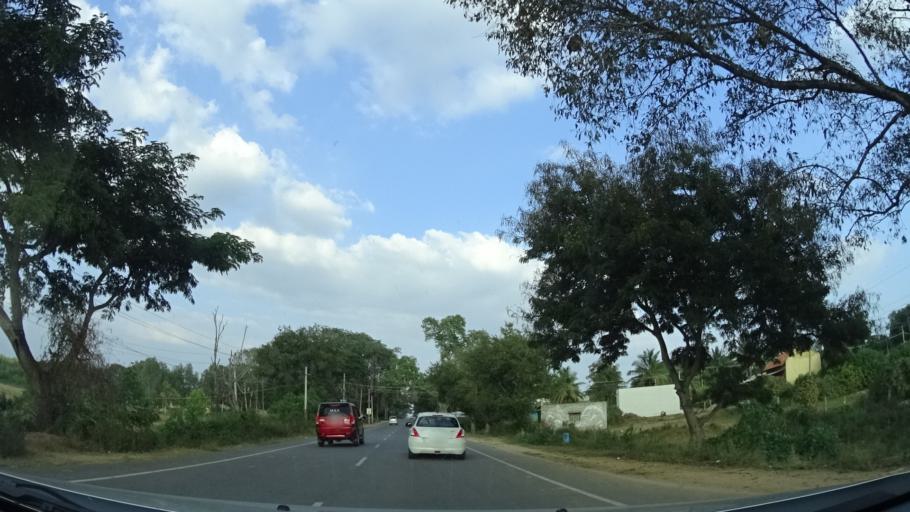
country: IN
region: Karnataka
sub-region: Mandya
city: Malavalli
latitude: 12.3757
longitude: 77.0356
